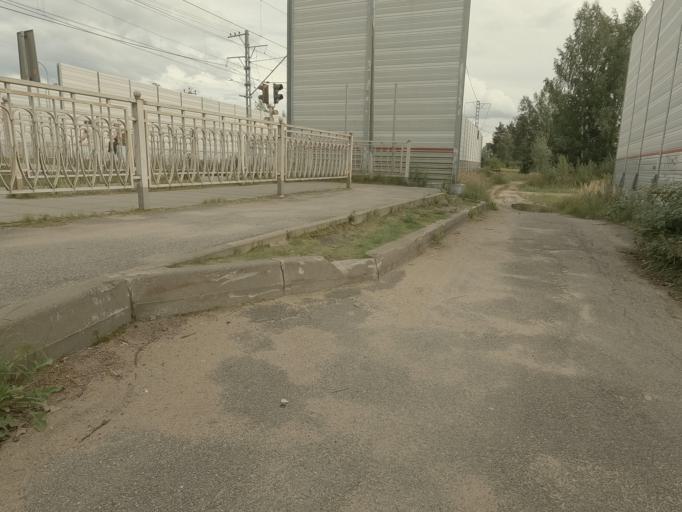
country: RU
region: Leningrad
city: Mga
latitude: 59.7595
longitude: 31.0380
